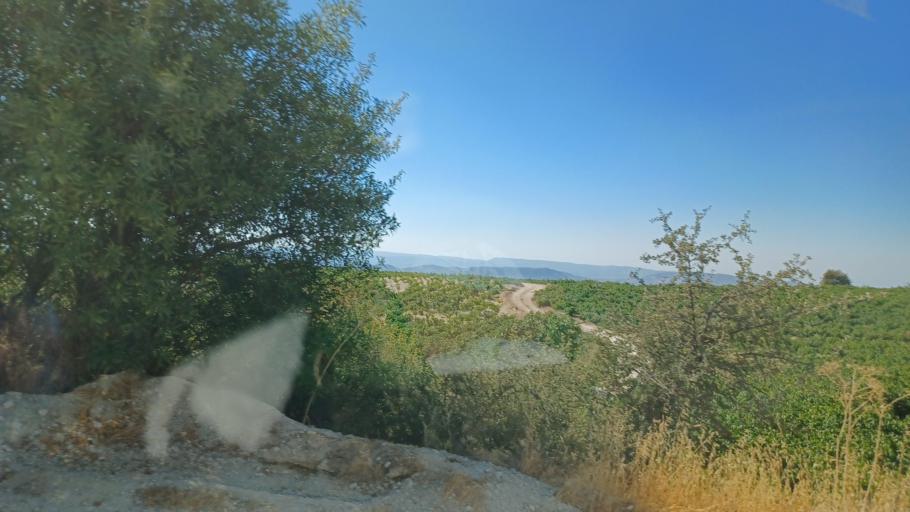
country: CY
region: Limassol
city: Pachna
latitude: 34.9059
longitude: 32.6416
